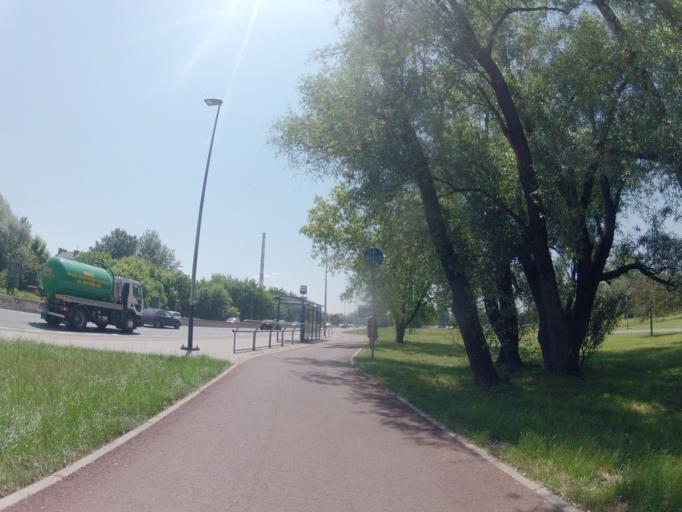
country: PL
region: Lesser Poland Voivodeship
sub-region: Krakow
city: Krakow
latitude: 50.0633
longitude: 20.0035
